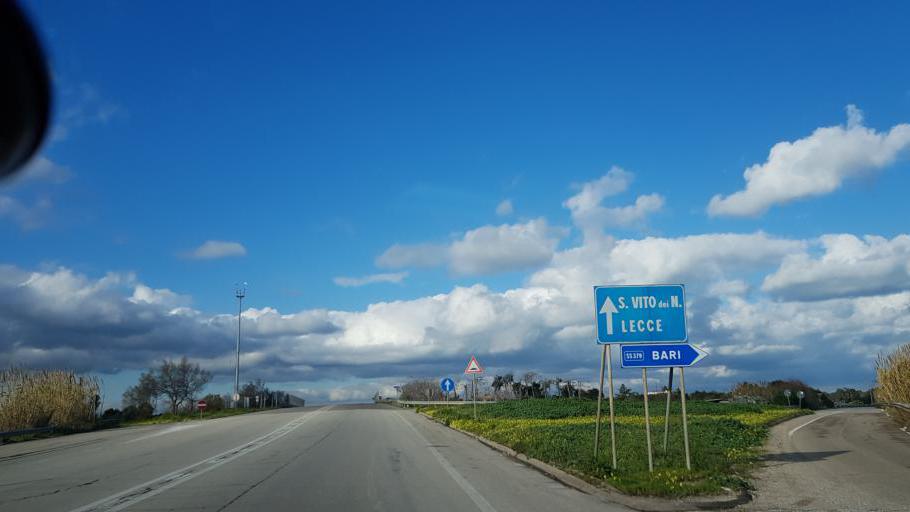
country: IT
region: Apulia
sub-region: Provincia di Brindisi
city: Brindisi
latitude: 40.6449
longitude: 17.9164
